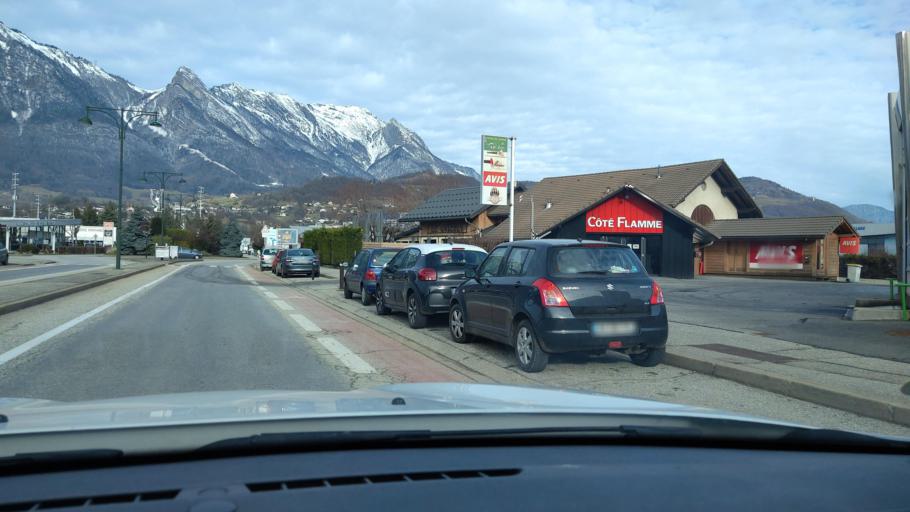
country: FR
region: Rhone-Alpes
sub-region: Departement de la Savoie
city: Grignon
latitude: 45.6604
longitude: 6.3742
